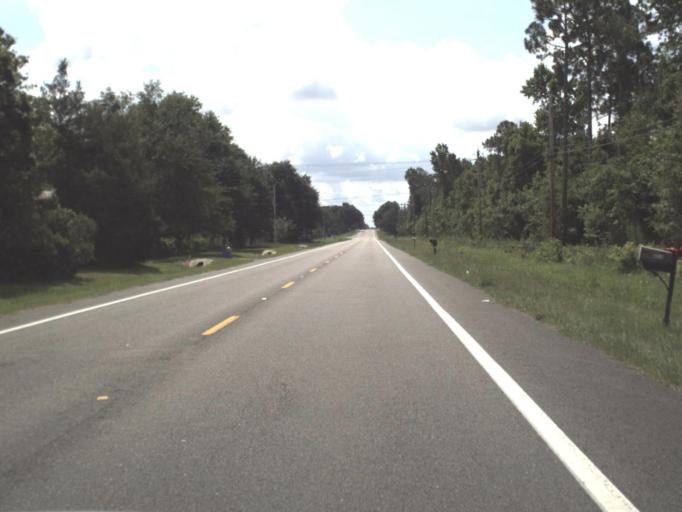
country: US
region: Florida
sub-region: Clay County
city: Green Cove Springs
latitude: 29.9879
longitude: -81.5726
